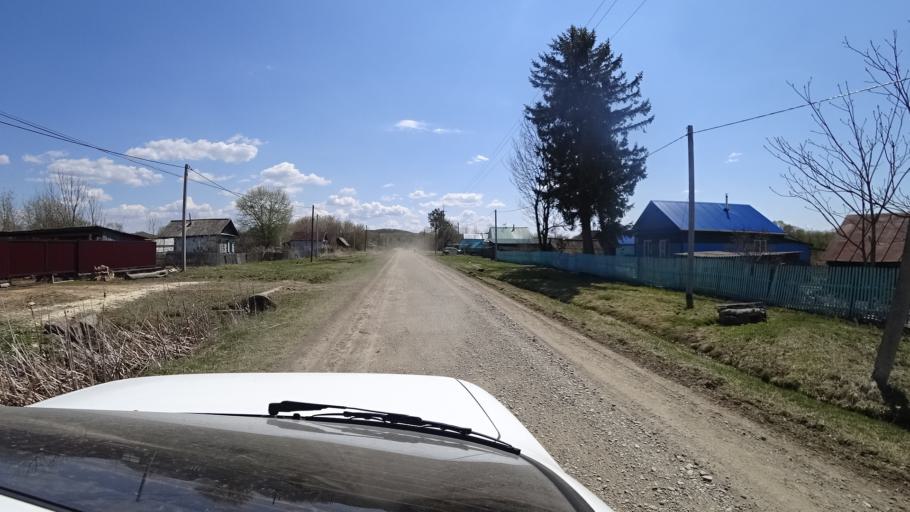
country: RU
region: Primorskiy
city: Lazo
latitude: 45.7922
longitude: 133.7642
